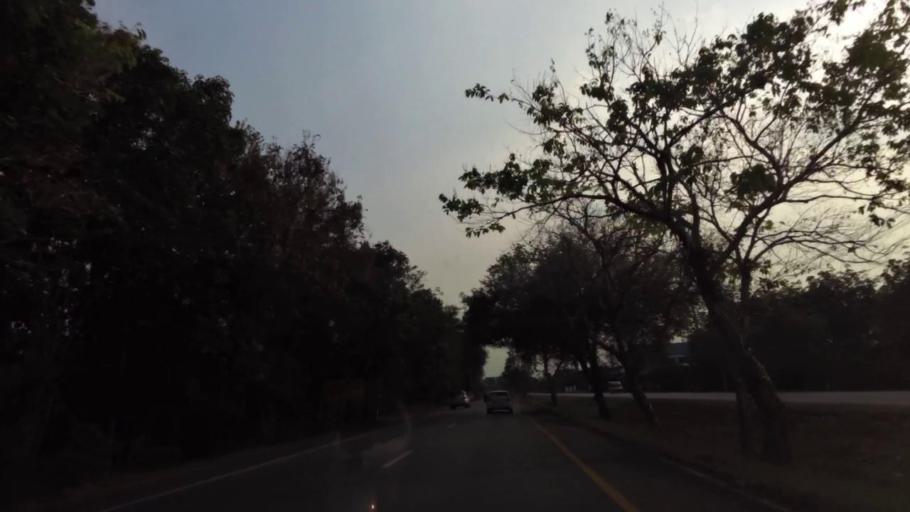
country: TH
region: Chanthaburi
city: Chanthaburi
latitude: 12.5343
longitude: 102.1575
